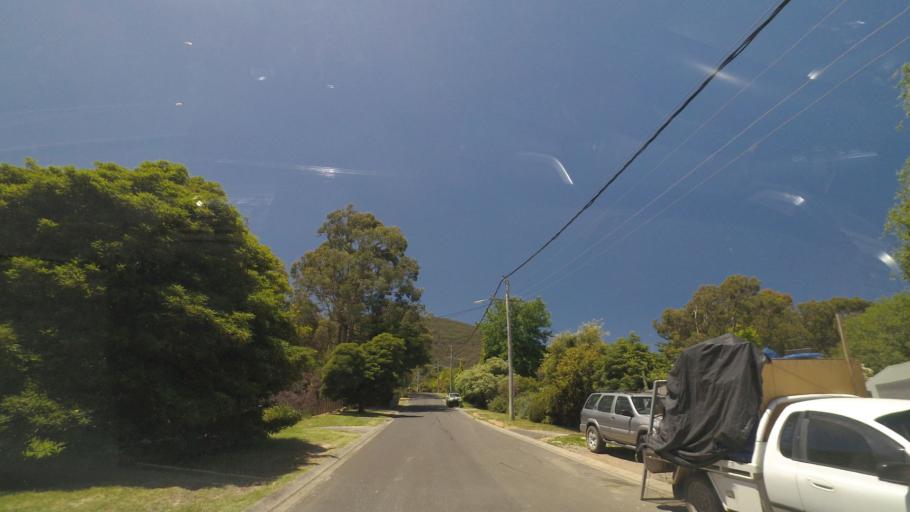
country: AU
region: Victoria
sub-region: Yarra Ranges
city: Montrose
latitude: -37.8177
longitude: 145.3426
